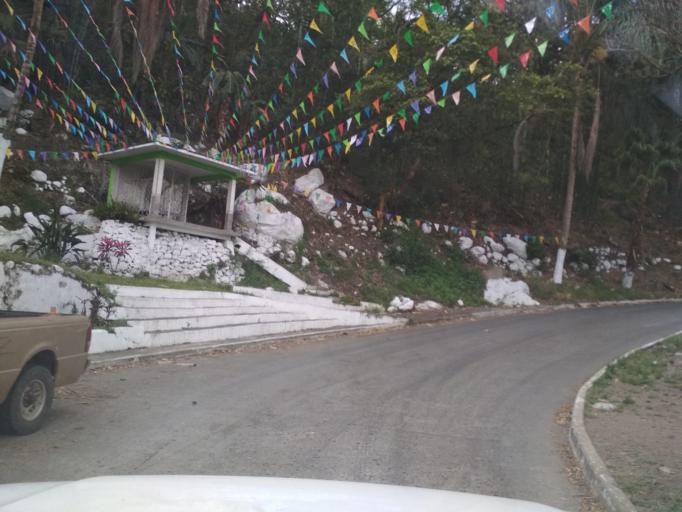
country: MX
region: Veracruz
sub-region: Cordoba
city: San Jose de Tapia
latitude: 18.8379
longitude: -96.9836
